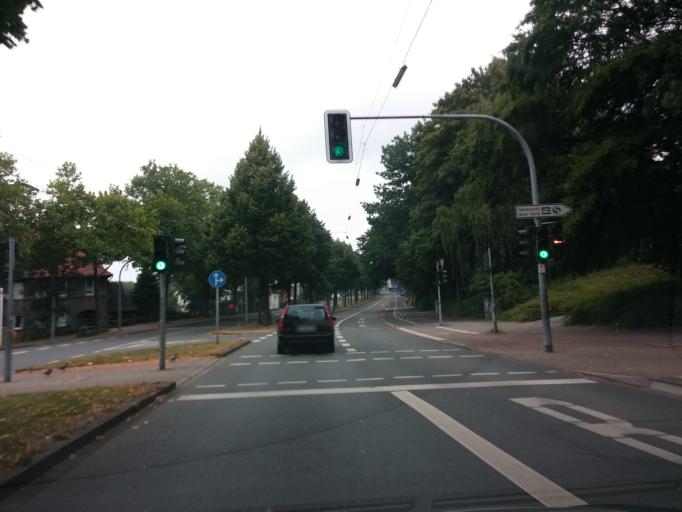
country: DE
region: North Rhine-Westphalia
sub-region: Regierungsbezirk Munster
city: Gladbeck
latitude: 51.5875
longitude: 7.0499
